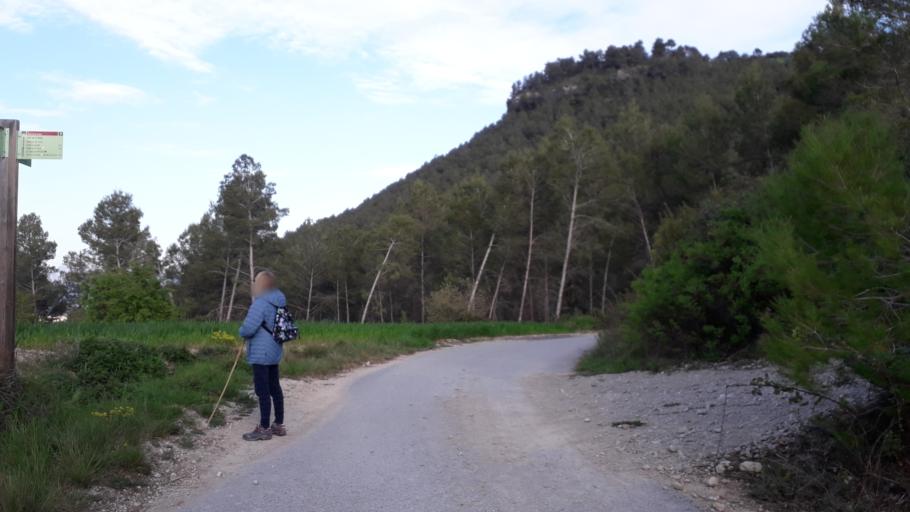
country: ES
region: Catalonia
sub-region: Provincia de Barcelona
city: Orpi
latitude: 41.5587
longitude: 1.5766
